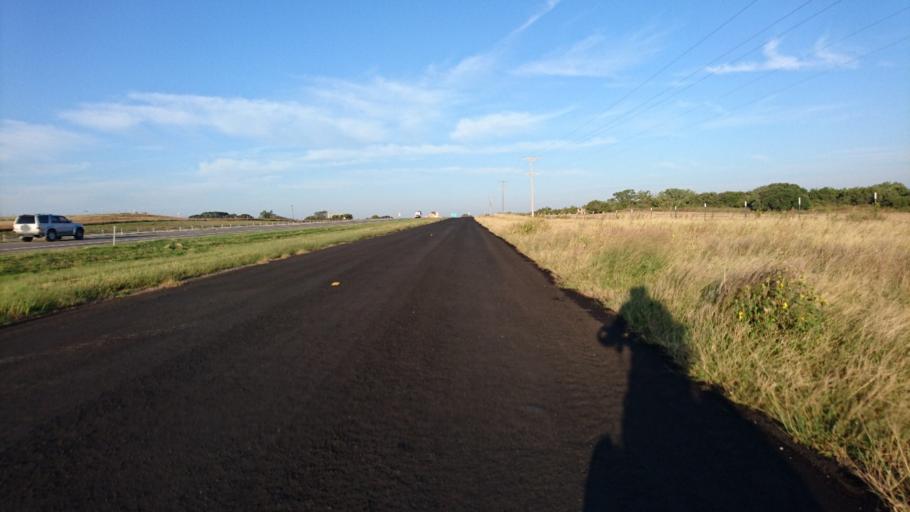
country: US
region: Oklahoma
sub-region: Beckham County
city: Sayre
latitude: 35.2625
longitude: -99.6958
